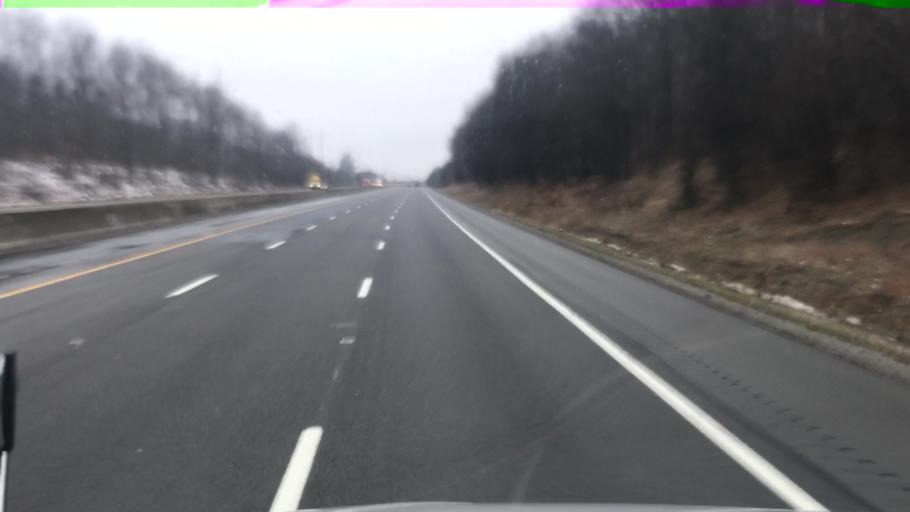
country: US
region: Ohio
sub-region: Cuyahoga County
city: Berea
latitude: 41.3433
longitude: -81.8465
